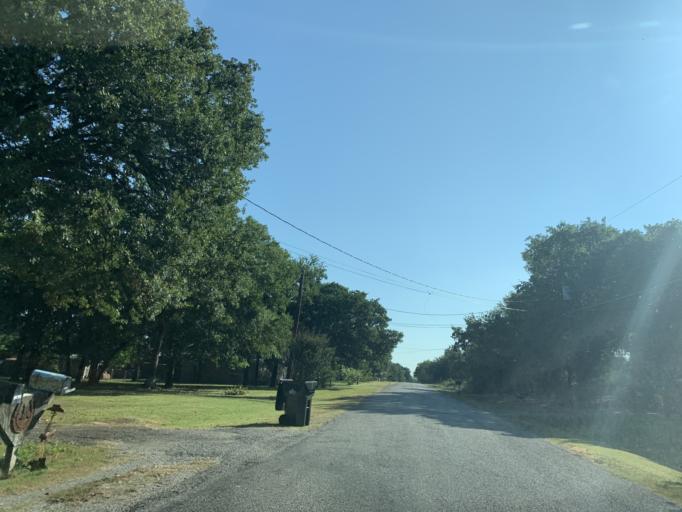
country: US
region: Texas
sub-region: Tarrant County
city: Lakeside
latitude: 32.8317
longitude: -97.4912
